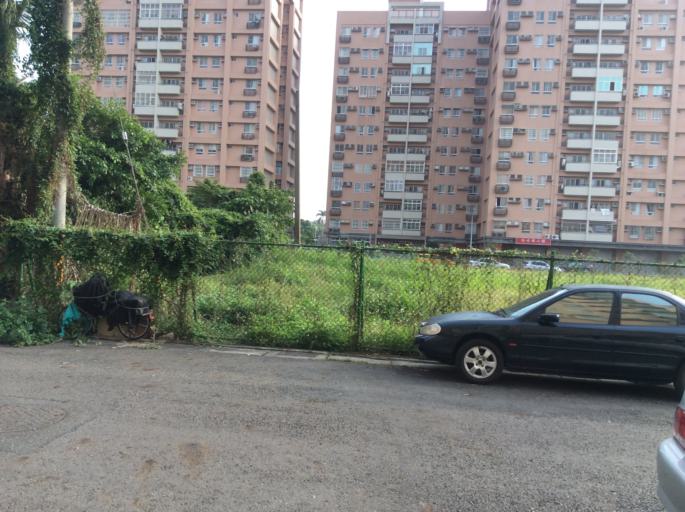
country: TW
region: Kaohsiung
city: Kaohsiung
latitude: 22.6962
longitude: 120.2870
